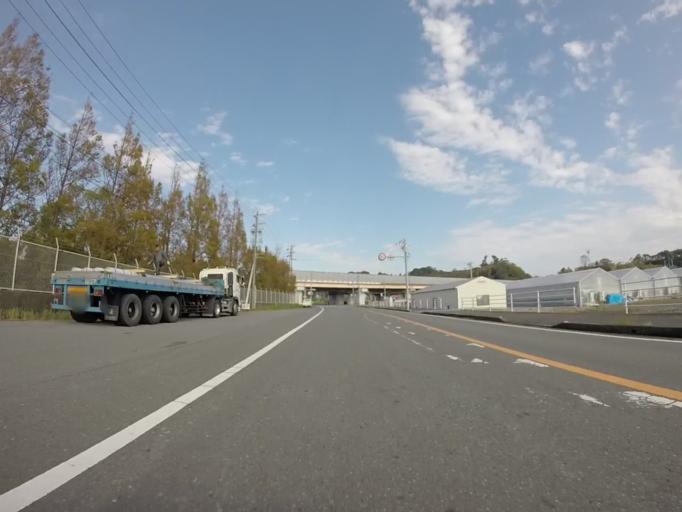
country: JP
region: Shizuoka
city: Shimada
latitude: 34.7743
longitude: 138.2287
